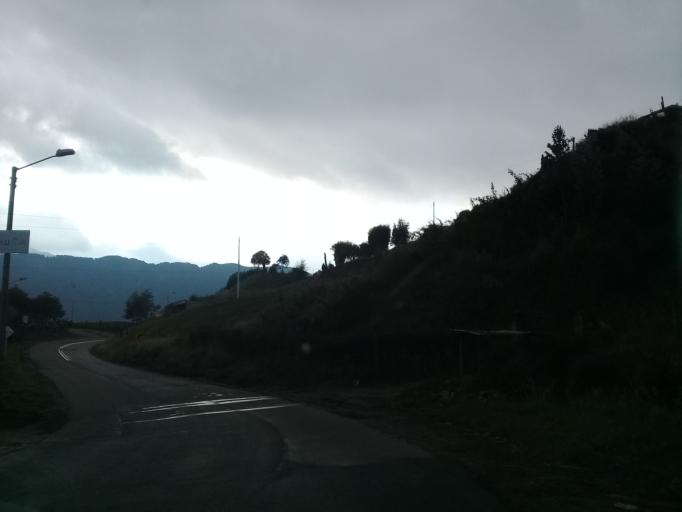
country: CO
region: Cundinamarca
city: Zipaquira
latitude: 5.0549
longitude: -74.0547
